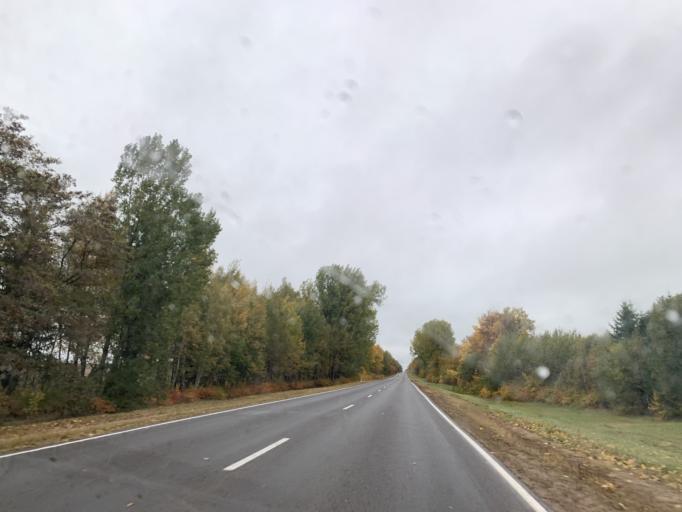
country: BY
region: Minsk
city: Haradzyeya
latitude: 53.4077
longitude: 26.6070
